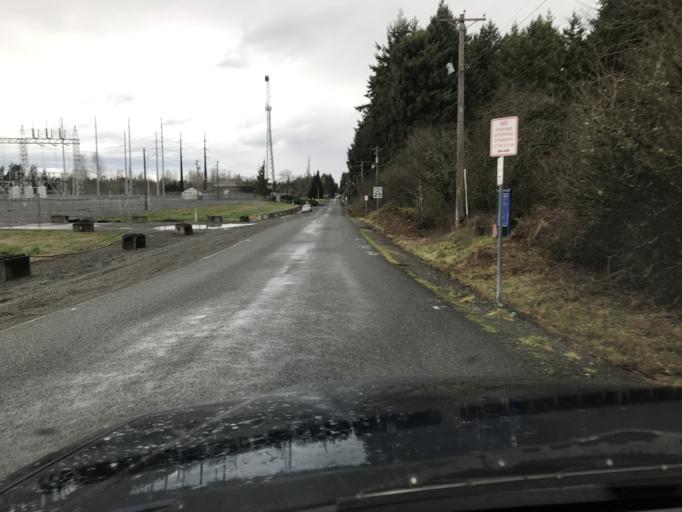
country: US
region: Washington
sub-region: Pierce County
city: Waller
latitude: 47.1810
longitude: -122.3678
